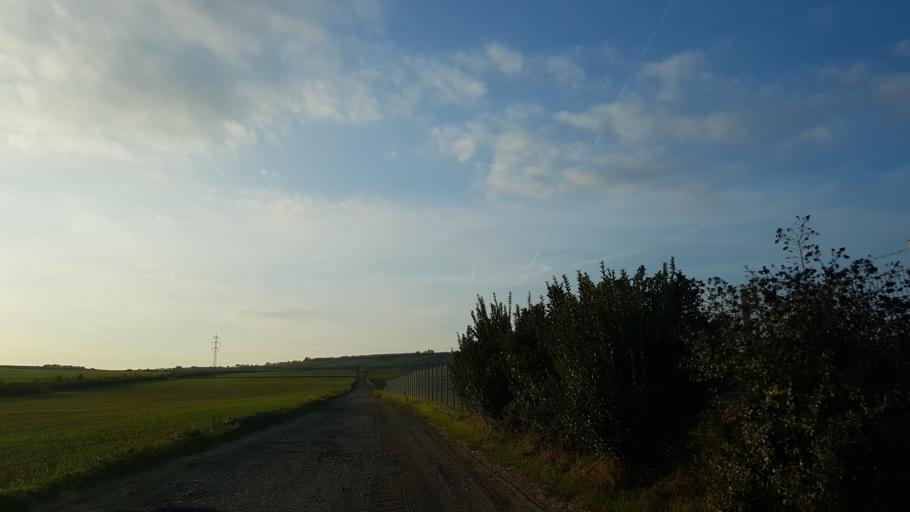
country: CZ
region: Zlin
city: Polesovice
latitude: 49.0196
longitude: 17.3486
